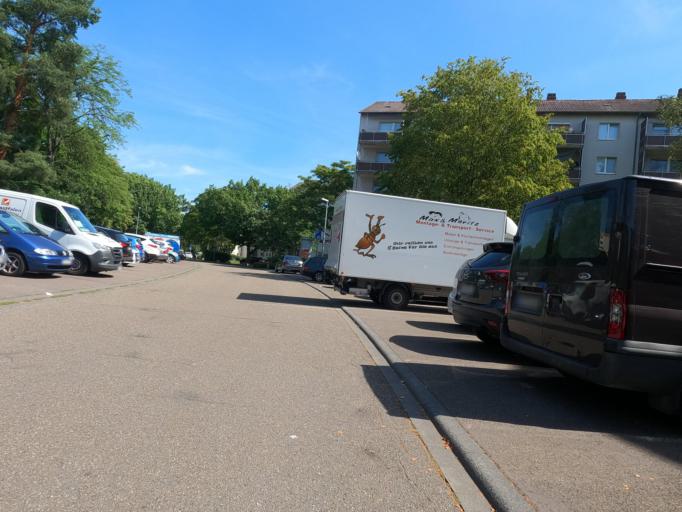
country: DE
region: Hesse
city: Dreieich
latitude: 50.0327
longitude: 8.6896
